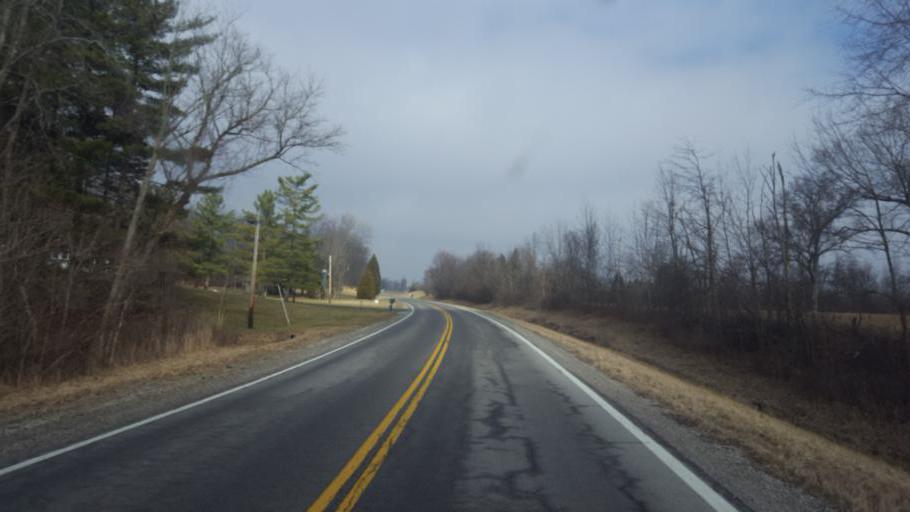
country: US
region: Ohio
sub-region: Crawford County
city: Bucyrus
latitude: 40.7492
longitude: -82.9061
